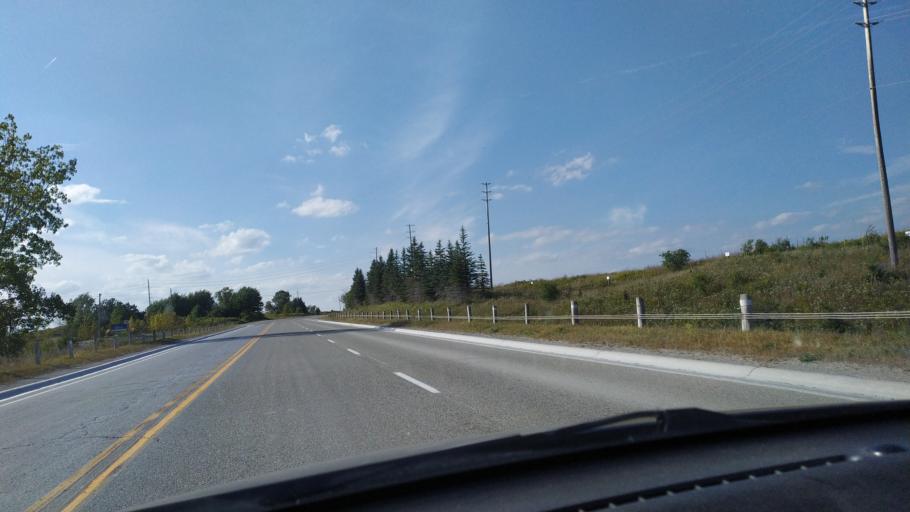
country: CA
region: Ontario
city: Ingersoll
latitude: 43.0724
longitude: -80.8556
